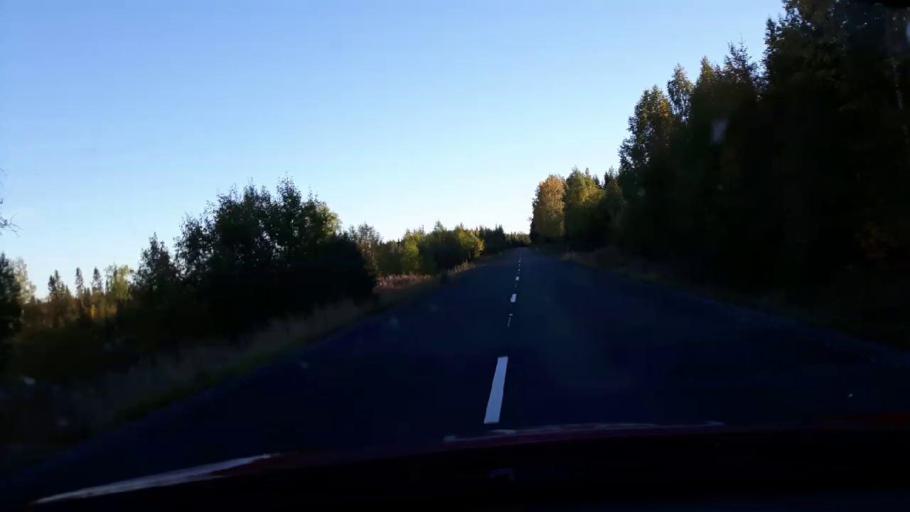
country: SE
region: Jaemtland
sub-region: OEstersunds Kommun
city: Lit
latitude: 63.4761
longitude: 14.8795
